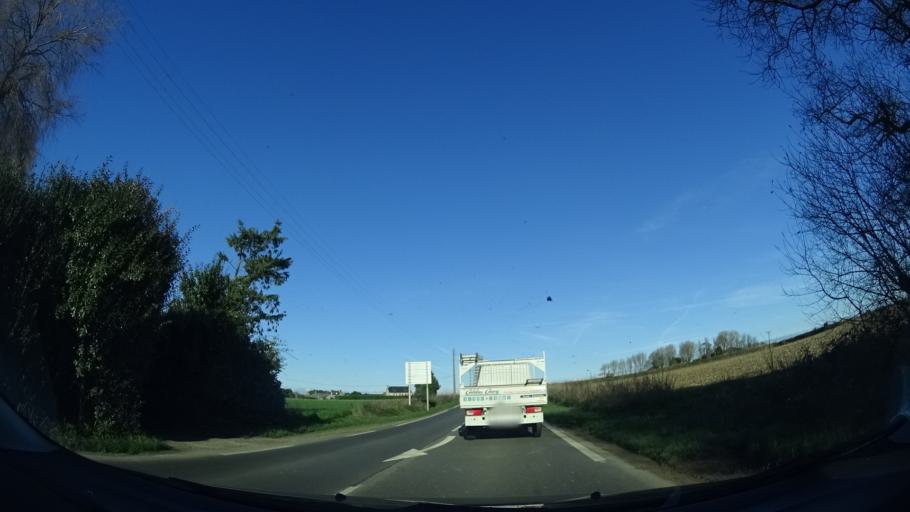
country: FR
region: Brittany
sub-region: Departement du Finistere
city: Saint-Pol-de-Leon
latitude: 48.6731
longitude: -4.0089
